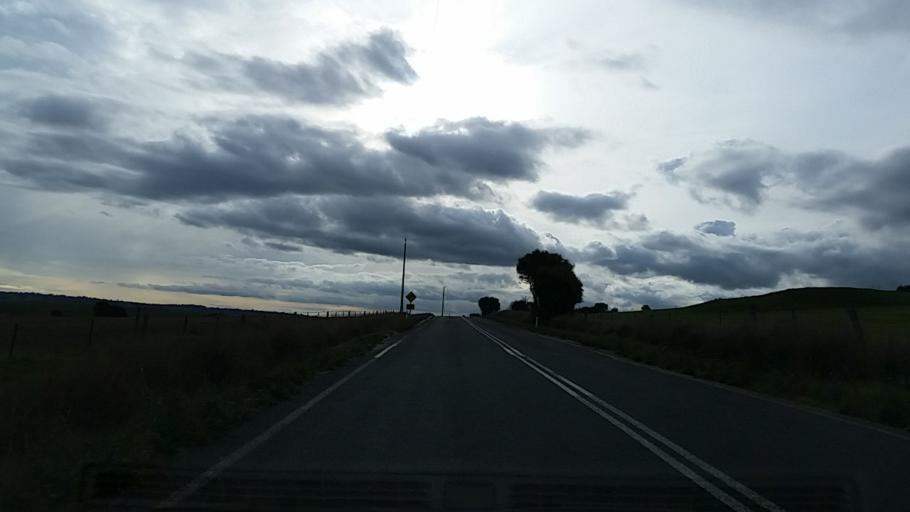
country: AU
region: South Australia
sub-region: Mount Barker
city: Callington
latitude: -35.0410
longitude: 139.0415
